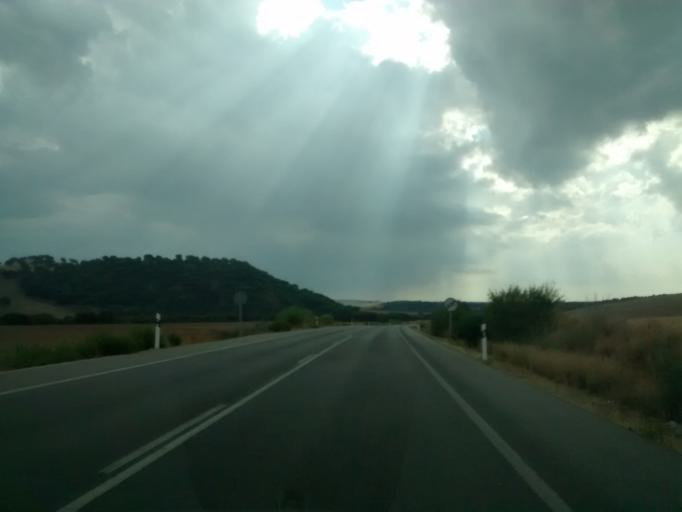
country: ES
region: Andalusia
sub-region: Provincia de Cadiz
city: Prado del Rey
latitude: 36.7489
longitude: -5.6130
